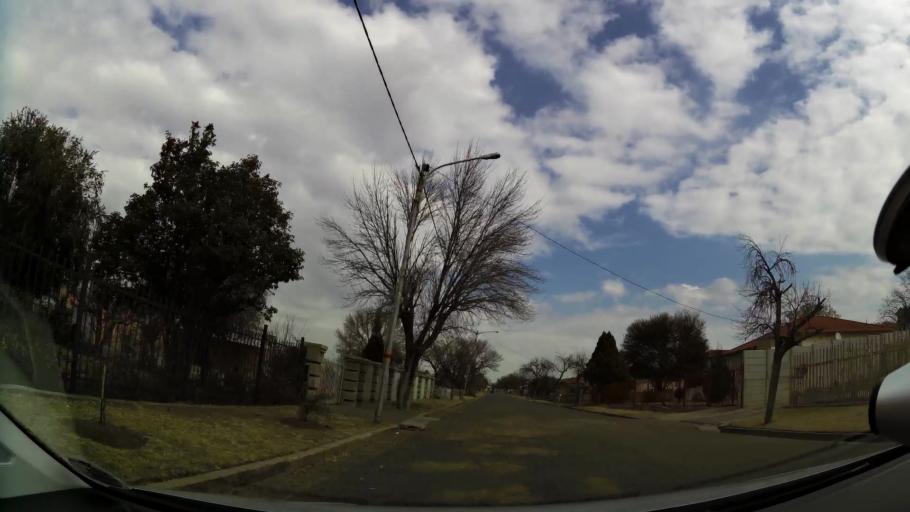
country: ZA
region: Orange Free State
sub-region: Fezile Dabi District Municipality
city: Kroonstad
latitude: -27.6524
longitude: 27.2374
